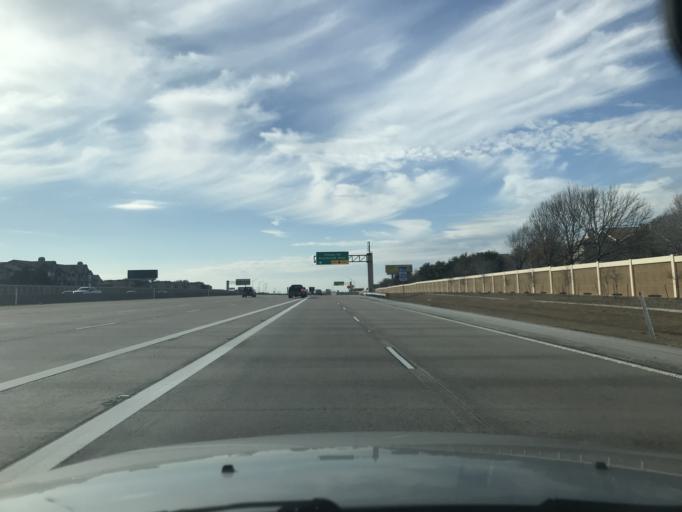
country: US
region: Texas
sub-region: Dallas County
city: Addison
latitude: 33.0130
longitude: -96.8359
